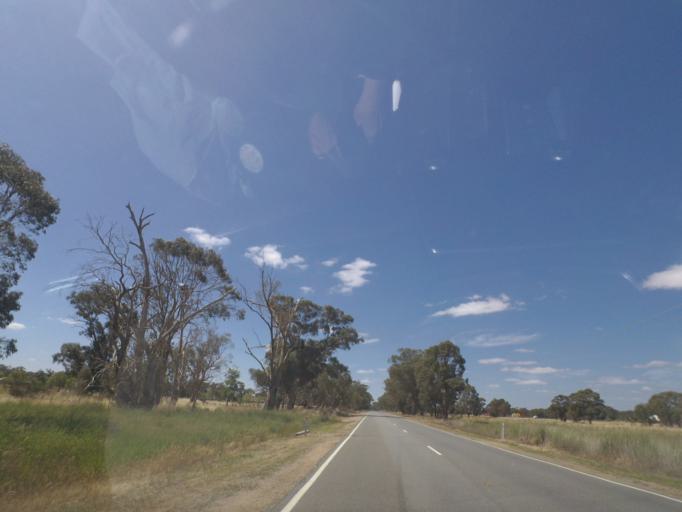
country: AU
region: Victoria
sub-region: Wangaratta
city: Wangaratta
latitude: -36.4163
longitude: 146.2648
